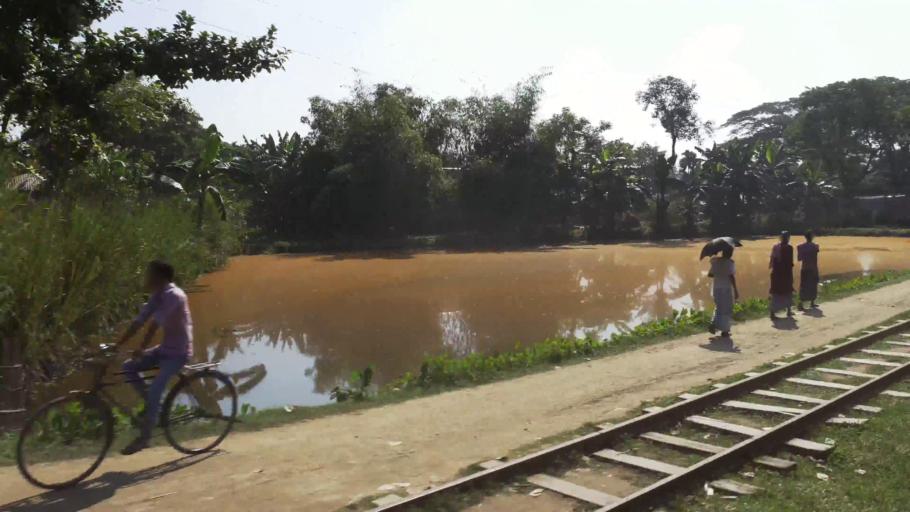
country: BD
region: Dhaka
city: Gafargaon
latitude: 24.4968
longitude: 90.5227
